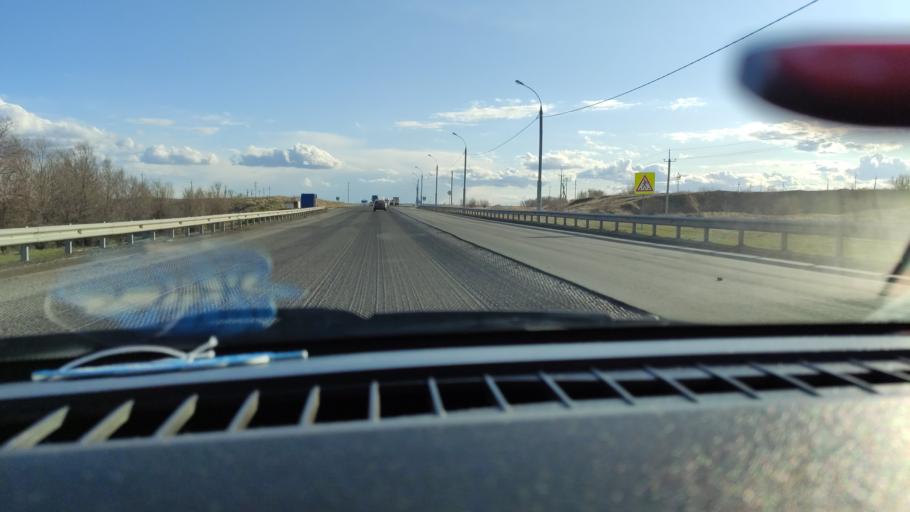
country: RU
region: Saratov
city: Yelshanka
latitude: 51.8158
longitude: 46.2094
